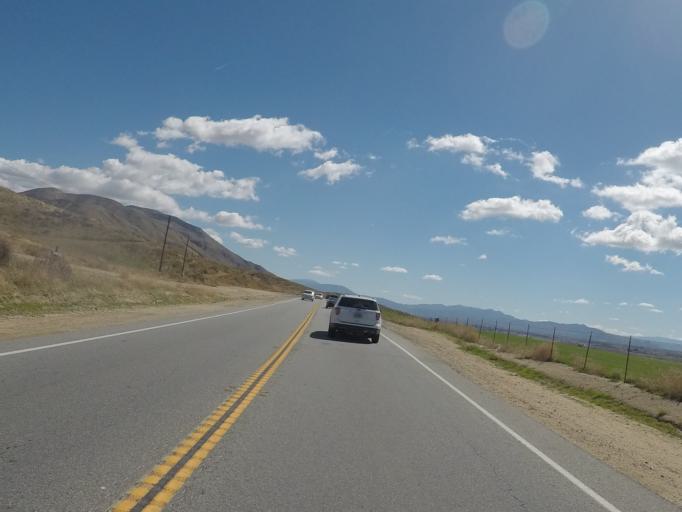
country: US
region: California
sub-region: Riverside County
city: Beaumont
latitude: 33.8538
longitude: -117.0160
